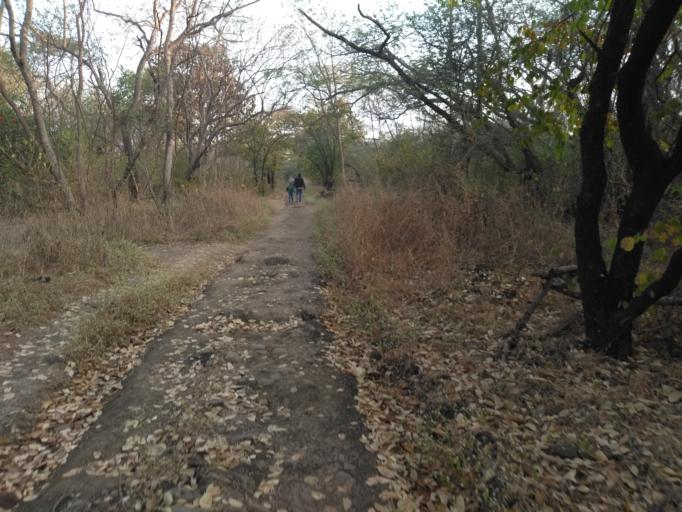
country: IN
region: Maharashtra
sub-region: Pune Division
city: Pune
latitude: 18.4710
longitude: 73.8400
